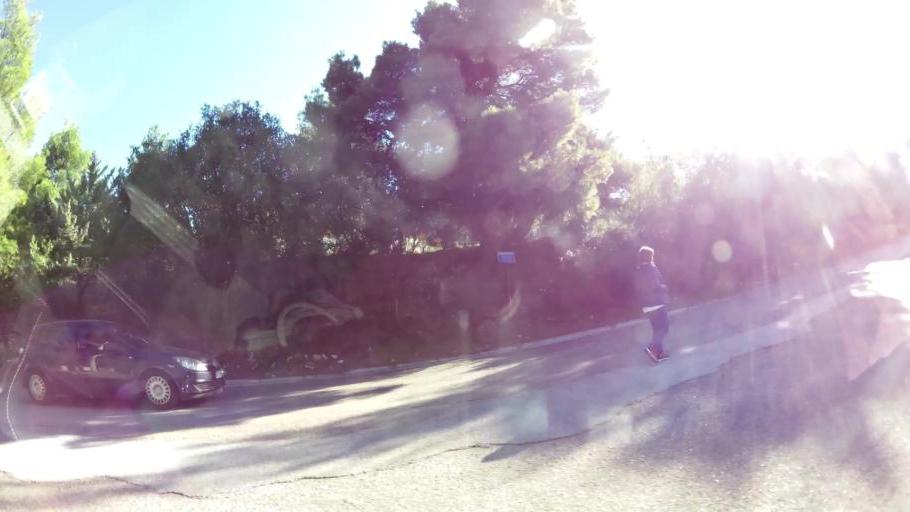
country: GR
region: Attica
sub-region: Nomarchia Athinas
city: Ekali
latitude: 38.1087
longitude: 23.8481
